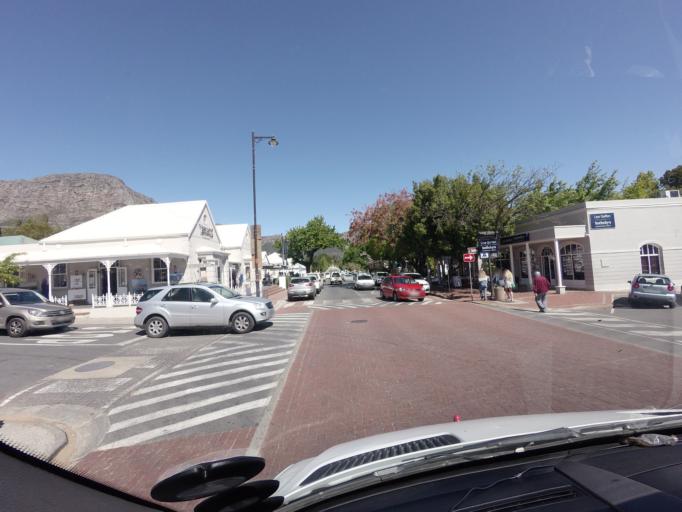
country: ZA
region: Western Cape
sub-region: Cape Winelands District Municipality
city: Paarl
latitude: -33.9113
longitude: 19.1200
